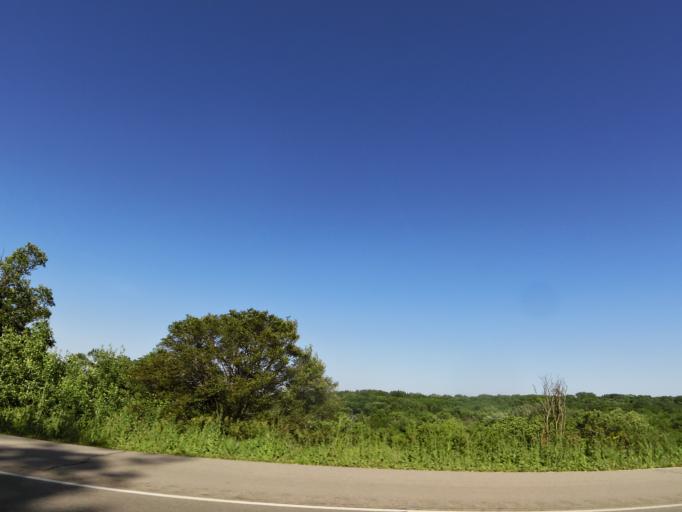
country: US
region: Wisconsin
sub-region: Rock County
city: Milton
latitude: 42.7493
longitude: -89.0044
